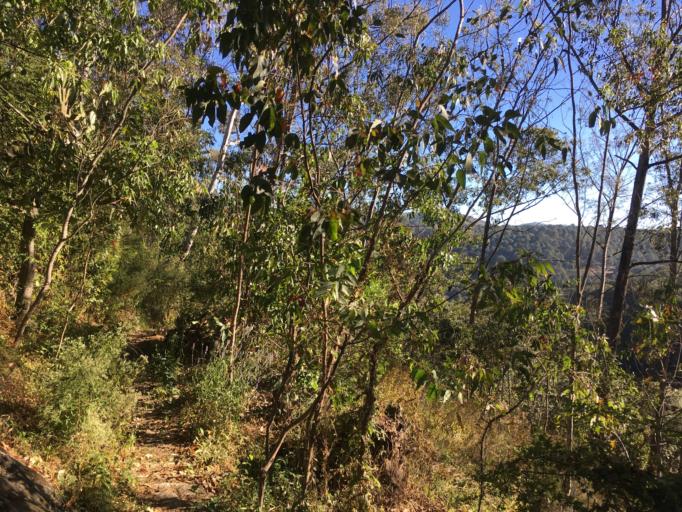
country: MX
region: Michoacan
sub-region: Morelia
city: Montana Monarca (Punta Altozano)
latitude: 19.6567
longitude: -101.1481
